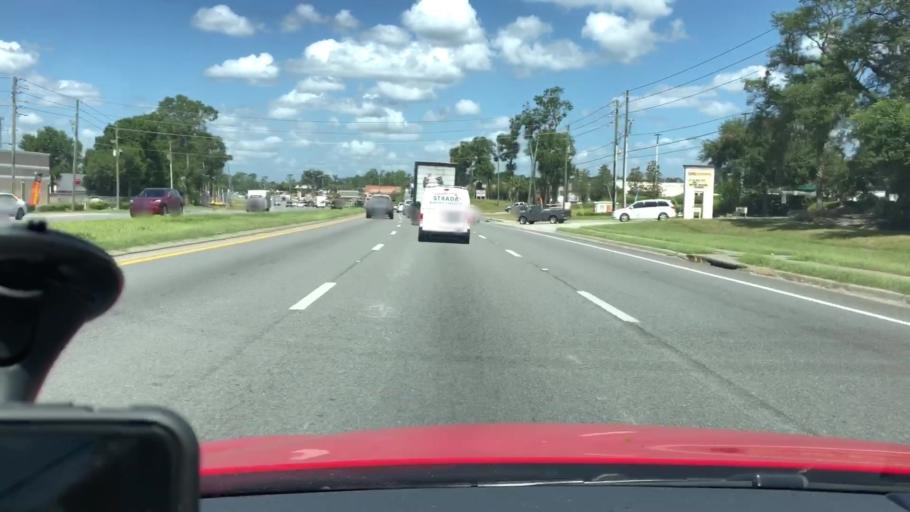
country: US
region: Florida
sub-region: Volusia County
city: De Land Southwest
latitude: 28.9849
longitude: -81.2994
